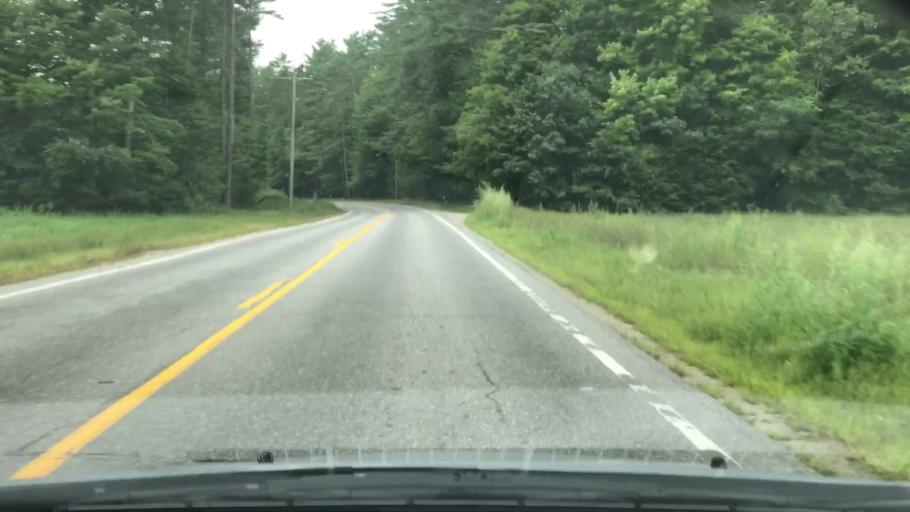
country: US
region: New Hampshire
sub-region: Grafton County
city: North Haverhill
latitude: 44.0702
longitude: -72.0393
